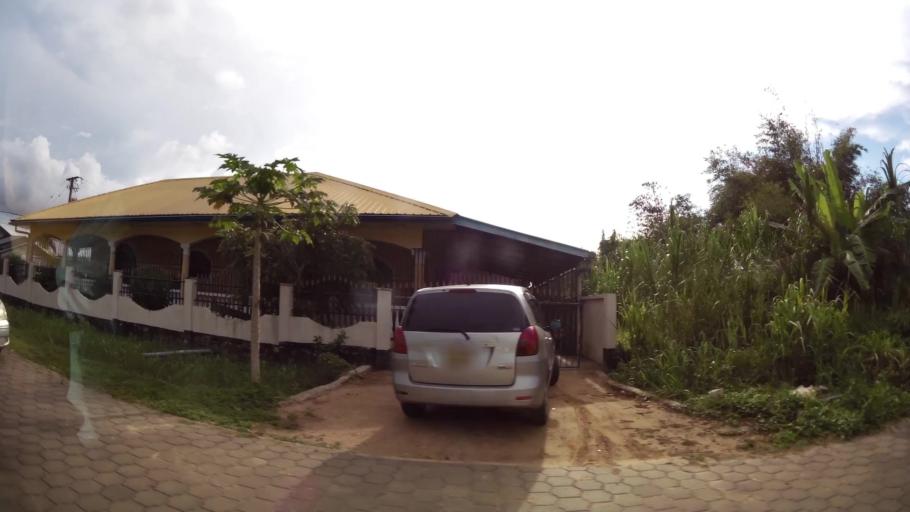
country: SR
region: Paramaribo
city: Paramaribo
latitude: 5.8482
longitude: -55.1773
